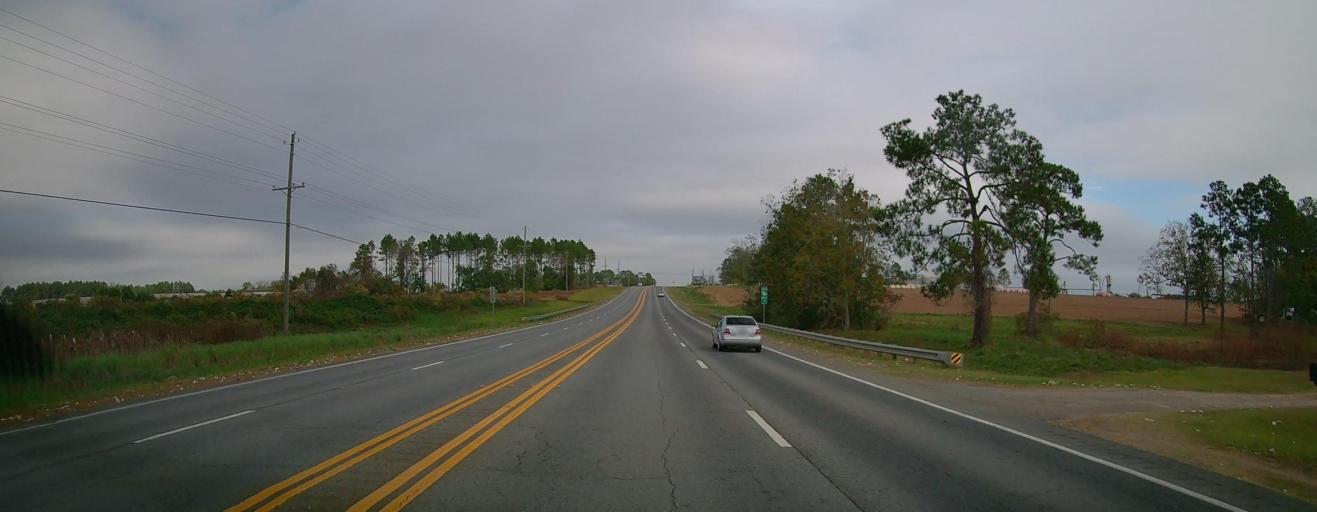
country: US
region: Georgia
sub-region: Tift County
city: Omega
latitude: 31.3703
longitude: -83.5707
